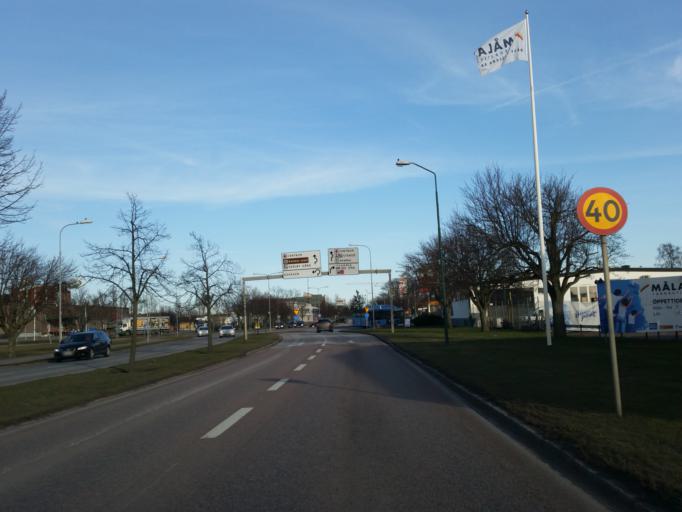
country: SE
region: Kalmar
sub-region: Kalmar Kommun
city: Kalmar
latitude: 56.6725
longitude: 16.3317
